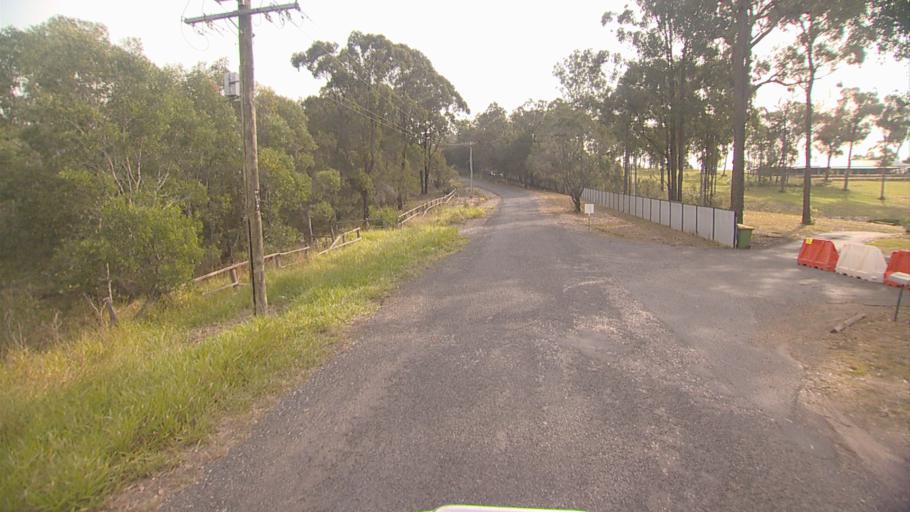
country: AU
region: Queensland
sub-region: Logan
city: Windaroo
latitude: -27.7299
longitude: 153.1610
